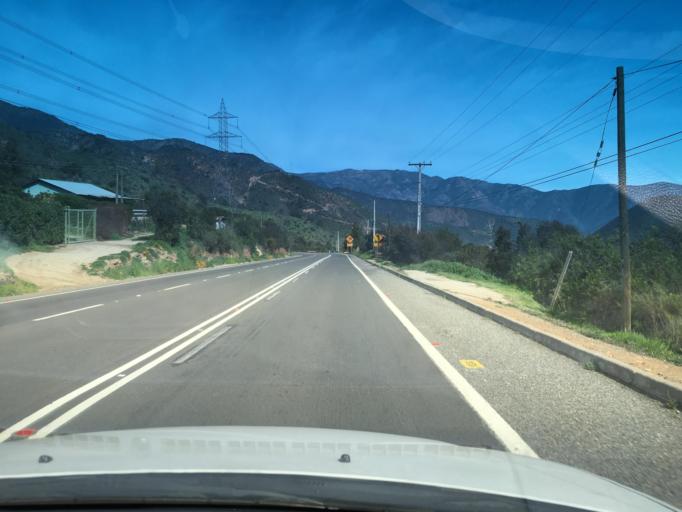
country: CL
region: Valparaiso
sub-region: Provincia de Marga Marga
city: Limache
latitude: -33.0577
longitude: -71.0430
